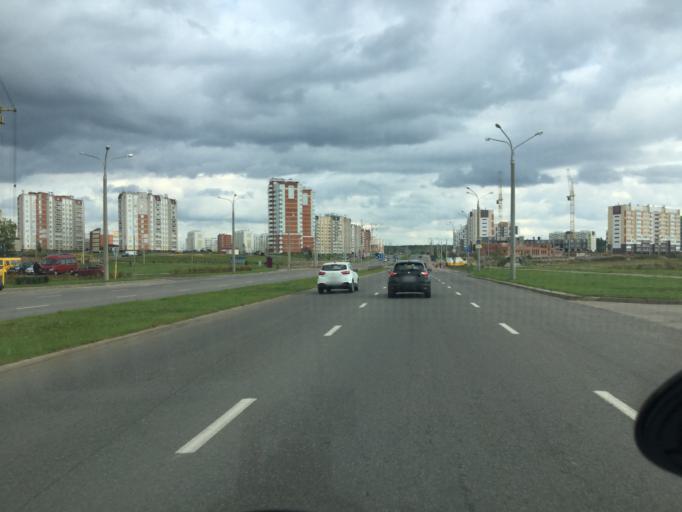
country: BY
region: Vitebsk
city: Vitebsk
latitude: 55.1655
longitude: 30.2617
